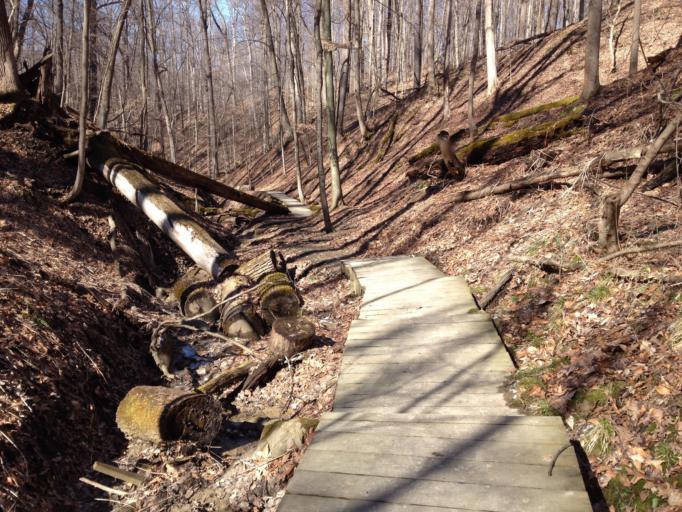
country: US
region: Ohio
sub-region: Summit County
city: Fairlawn
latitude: 41.1656
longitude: -81.5579
